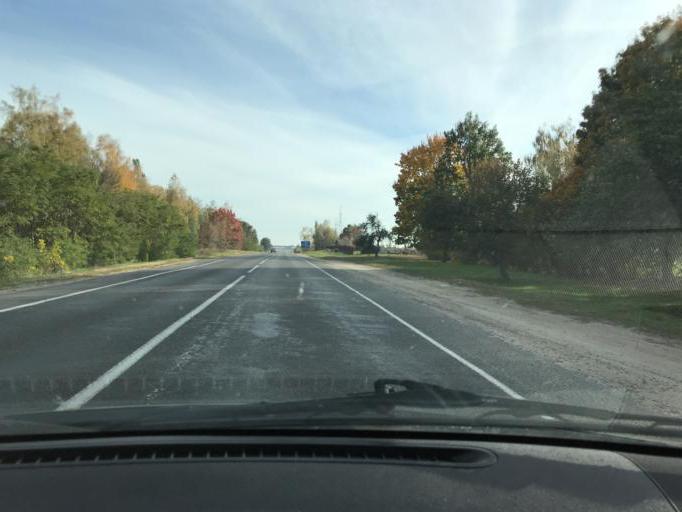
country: BY
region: Brest
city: Asnyezhytsy
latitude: 52.1929
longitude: 26.0722
